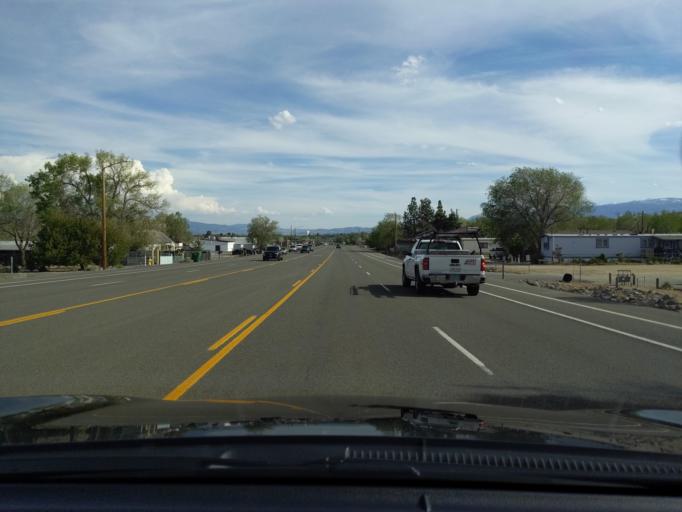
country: US
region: Nevada
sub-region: Washoe County
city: Sun Valley
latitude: 39.5951
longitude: -119.7806
